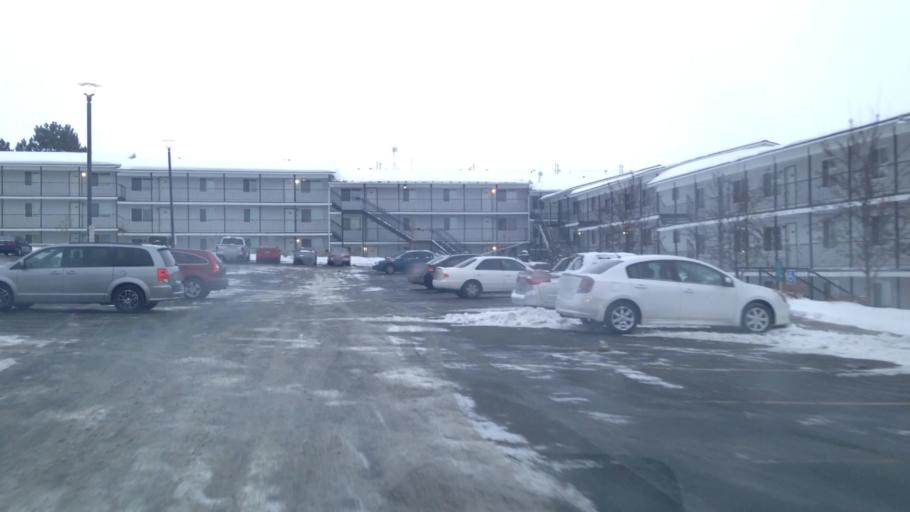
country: US
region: Idaho
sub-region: Madison County
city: Rexburg
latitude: 43.8174
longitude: -111.7874
